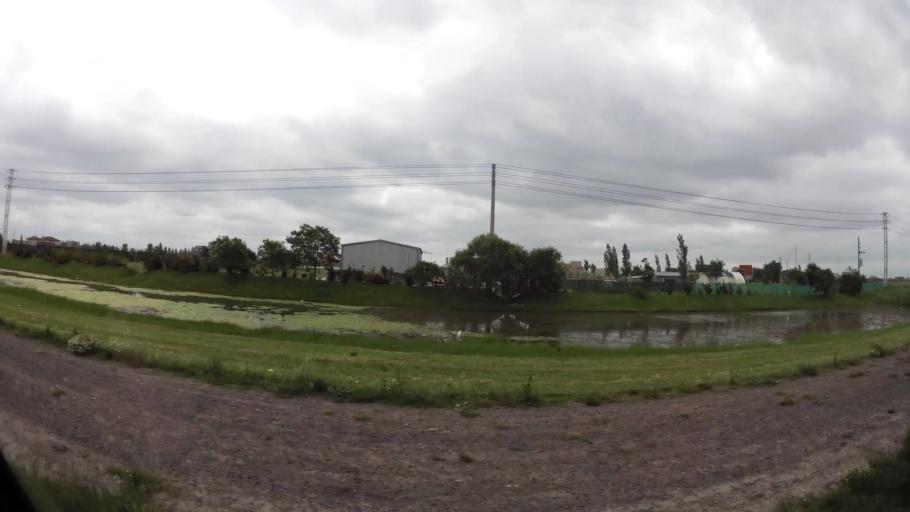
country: AR
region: Buenos Aires
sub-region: Partido de San Vicente
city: San Vicente
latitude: -34.9681
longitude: -58.4673
